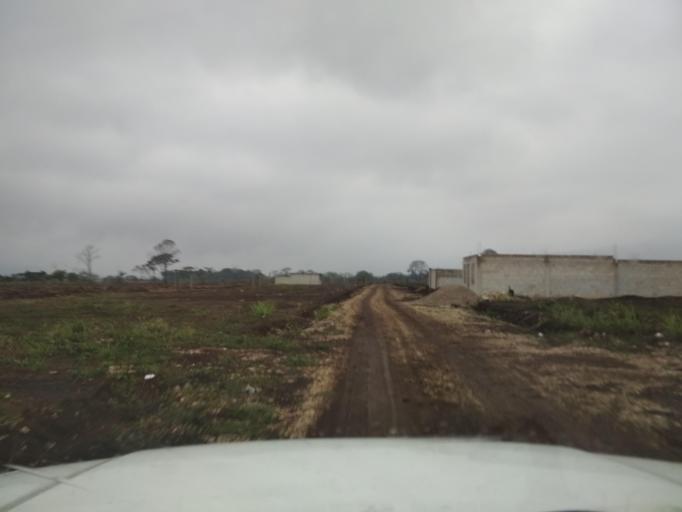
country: MX
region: Veracruz
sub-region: Cordoba
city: Veinte de Noviembre
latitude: 18.8590
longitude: -96.9611
